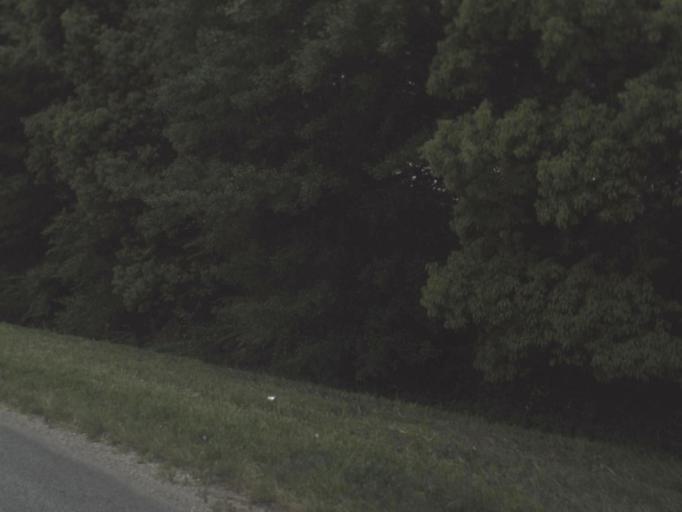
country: US
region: Florida
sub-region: Escambia County
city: Ensley
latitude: 30.5466
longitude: -87.2827
